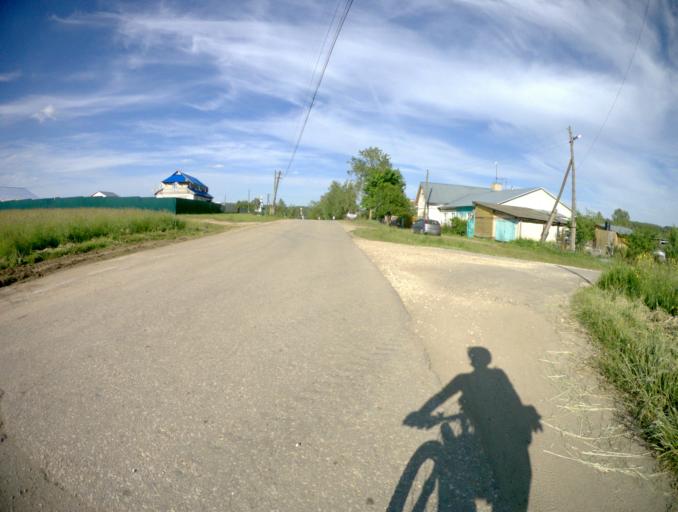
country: RU
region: Vladimir
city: Vorsha
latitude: 56.1702
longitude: 40.1571
